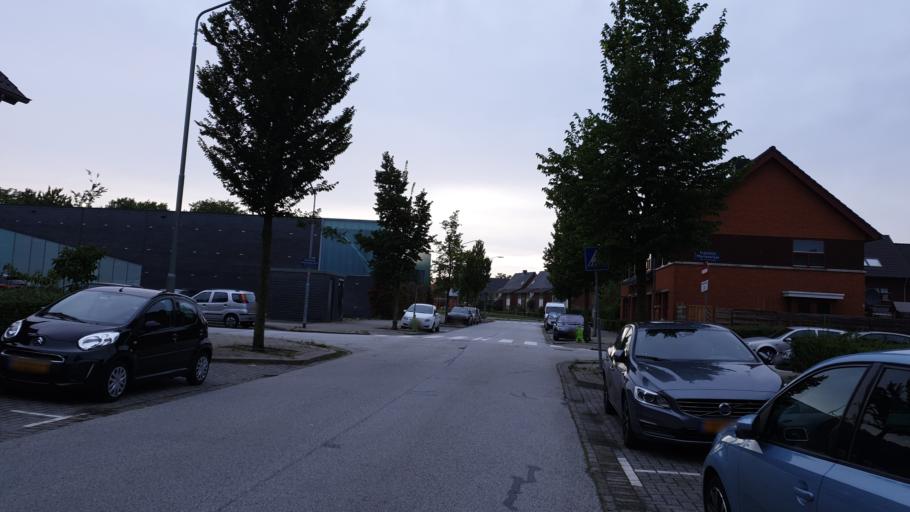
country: NL
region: South Holland
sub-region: Gemeente Dordrecht
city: Dordrecht
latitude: 51.7980
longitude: 4.6619
